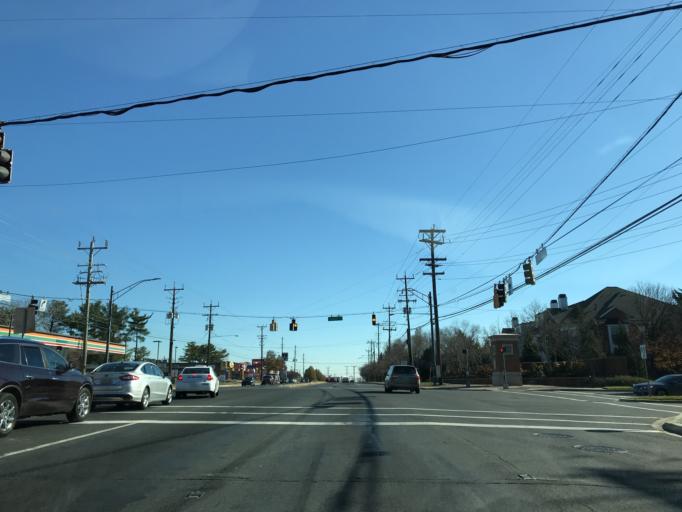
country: US
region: Maryland
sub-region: Montgomery County
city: Derwood
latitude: 39.1158
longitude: -77.1666
